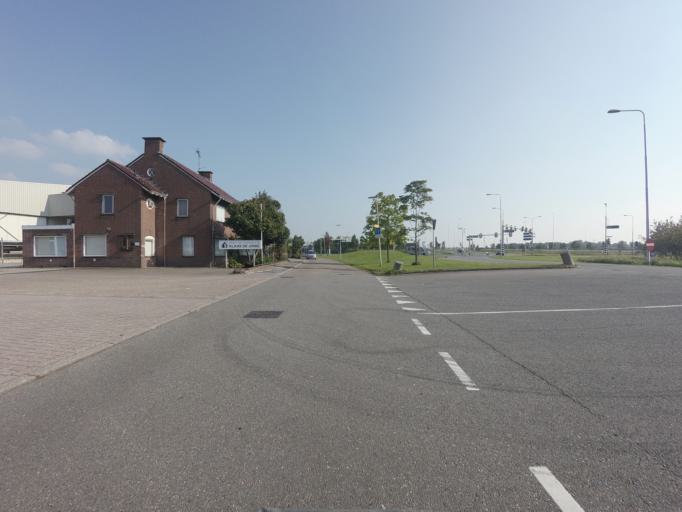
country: NL
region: Utrecht
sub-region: Gemeente Bunnik
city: Bunnik
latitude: 52.0614
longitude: 5.2120
